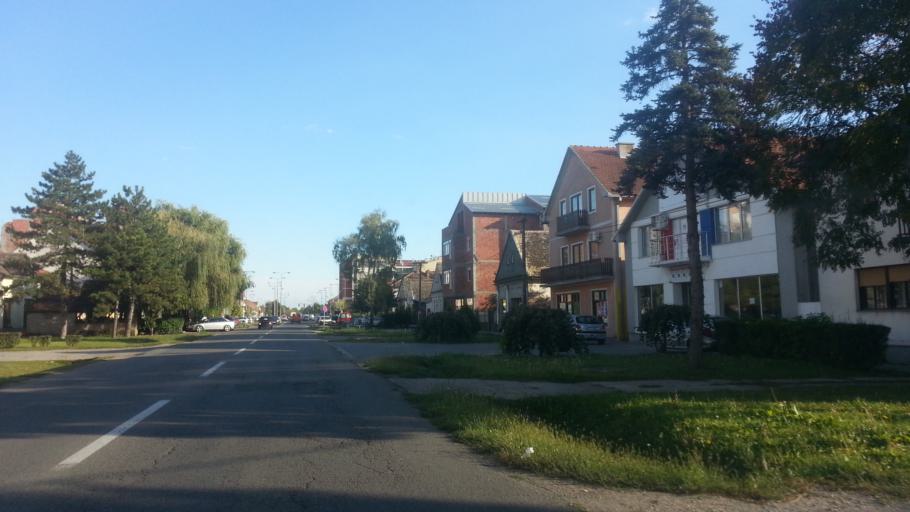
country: RS
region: Autonomna Pokrajina Vojvodina
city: Nova Pazova
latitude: 44.9463
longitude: 20.2164
